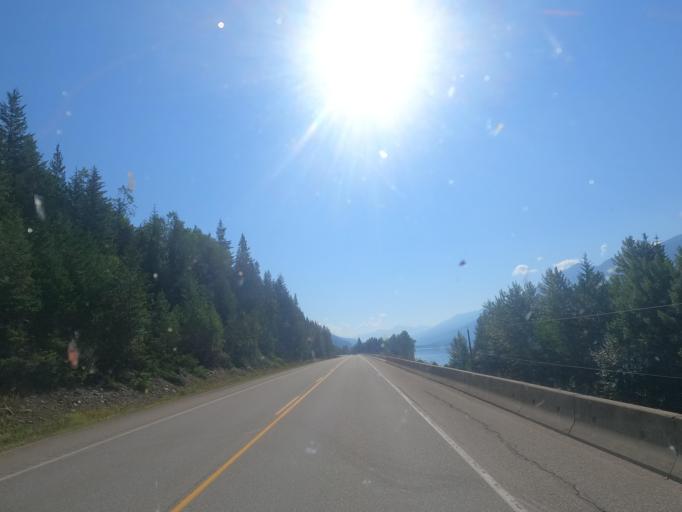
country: CA
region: Alberta
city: Jasper Park Lodge
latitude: 52.9579
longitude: -118.8989
